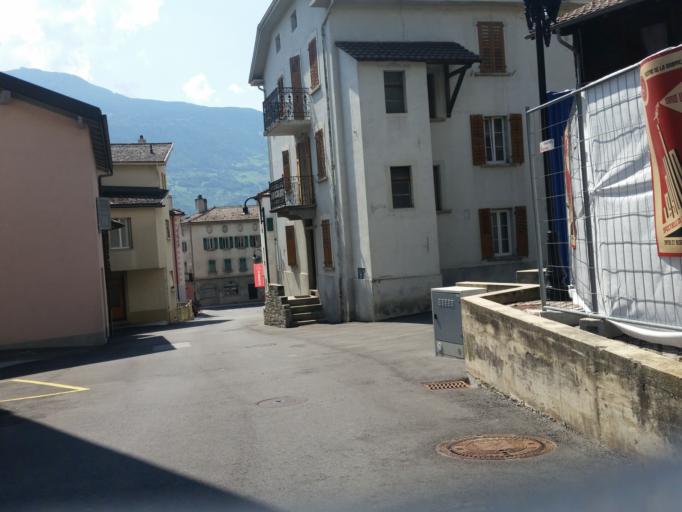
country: CH
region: Valais
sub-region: Conthey District
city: Vetroz
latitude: 46.2266
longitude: 7.2822
